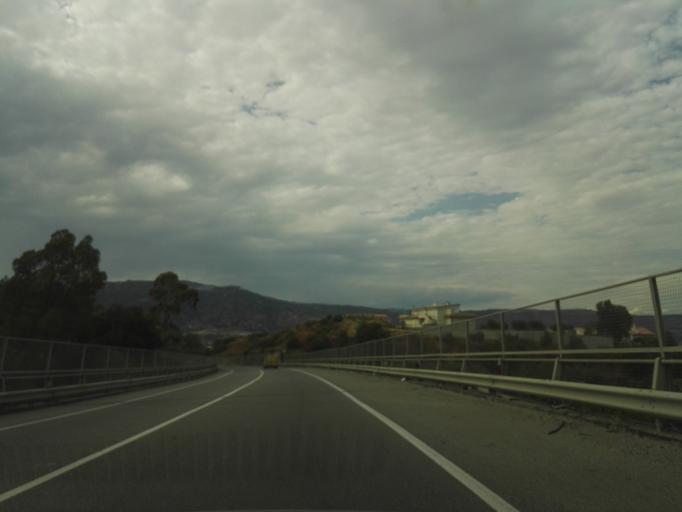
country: IT
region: Calabria
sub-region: Provincia di Catanzaro
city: Soverato Superiore
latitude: 38.6972
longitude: 16.5377
